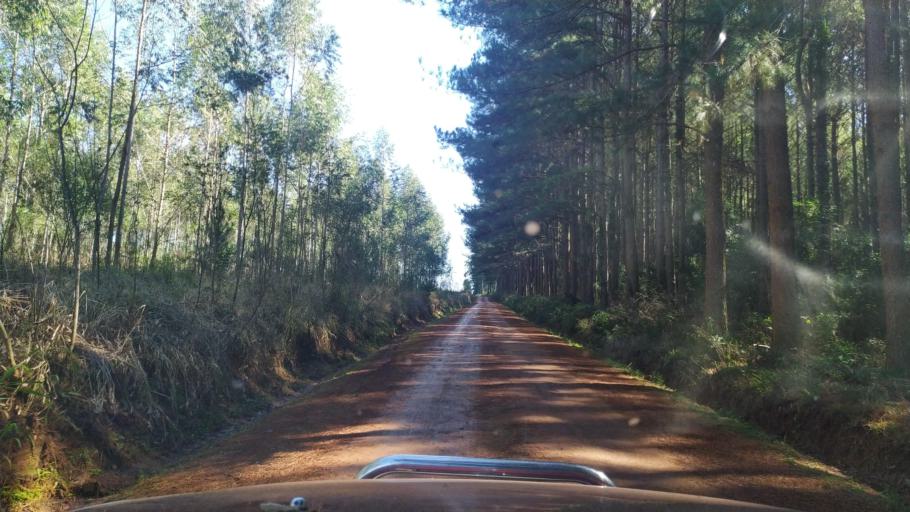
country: AR
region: Misiones
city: El Alcazar
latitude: -26.7344
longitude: -54.6569
